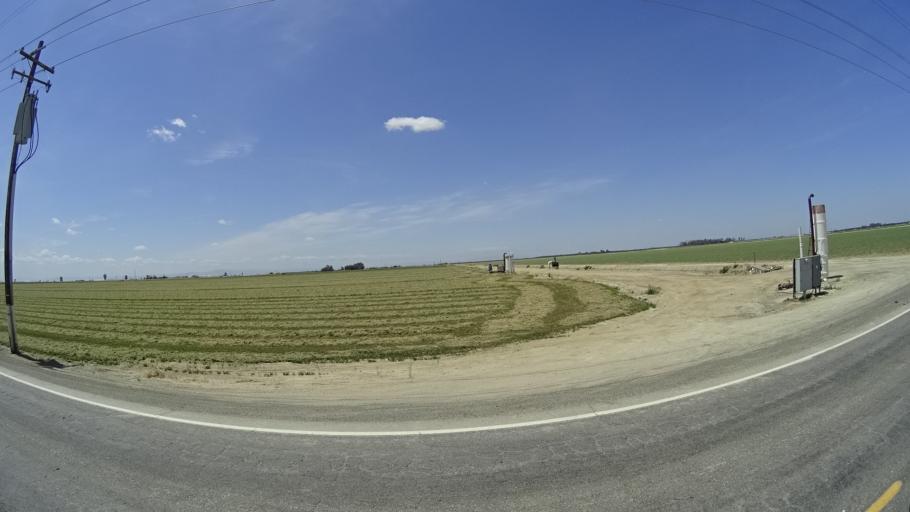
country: US
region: California
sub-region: Kings County
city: Home Garden
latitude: 36.2400
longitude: -119.6549
